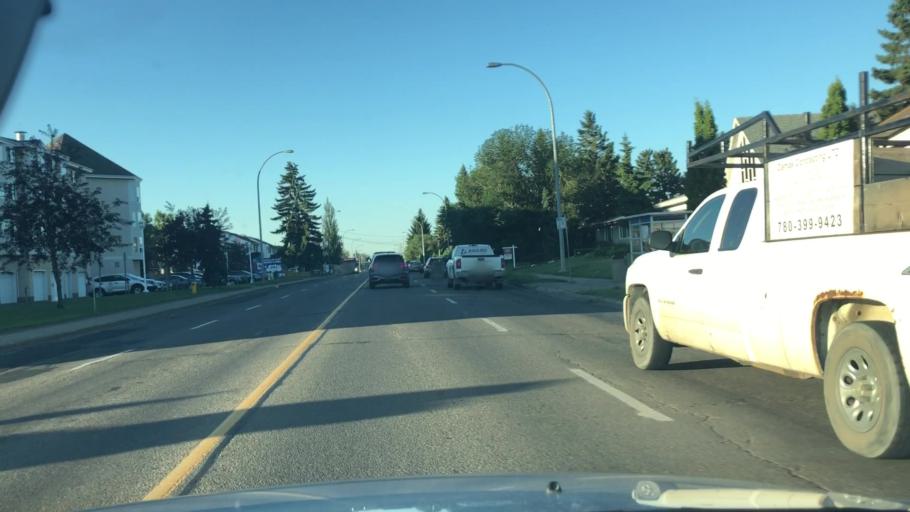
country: CA
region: Alberta
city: Edmonton
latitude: 53.5963
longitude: -113.5412
